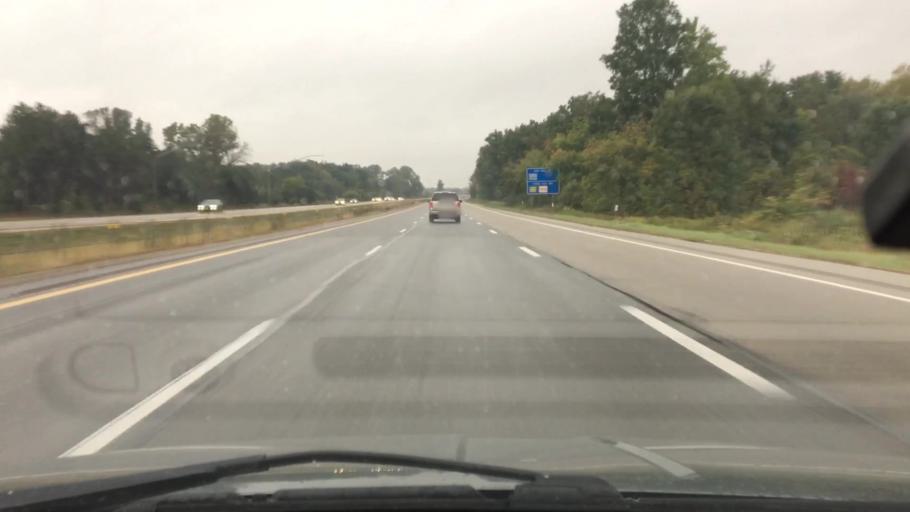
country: US
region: Michigan
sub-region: Jackson County
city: Grass Lake
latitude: 42.2926
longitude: -84.1832
